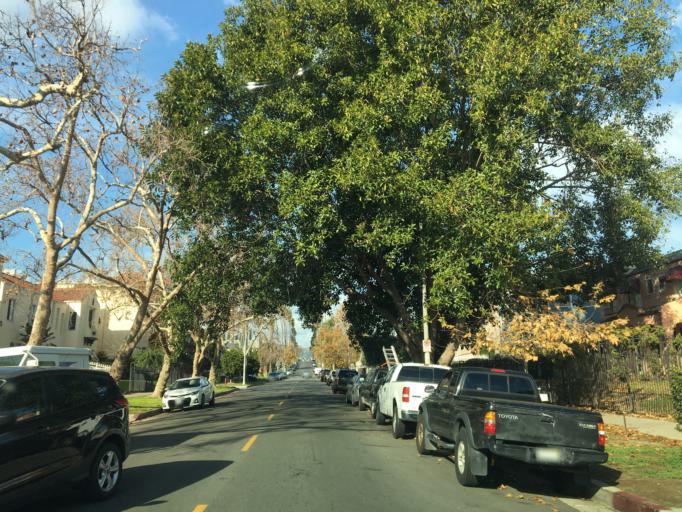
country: US
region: California
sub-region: Los Angeles County
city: Silver Lake
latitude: 34.0711
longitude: -118.2954
